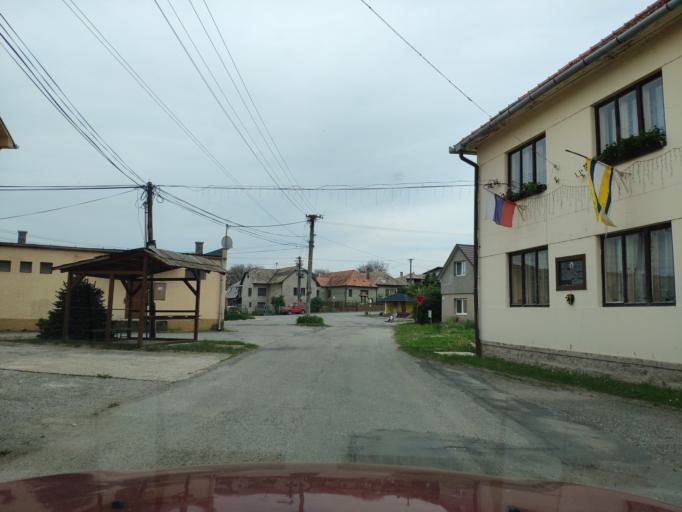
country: SK
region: Banskobystricky
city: Rimavska Sobota
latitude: 48.4816
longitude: 20.0716
